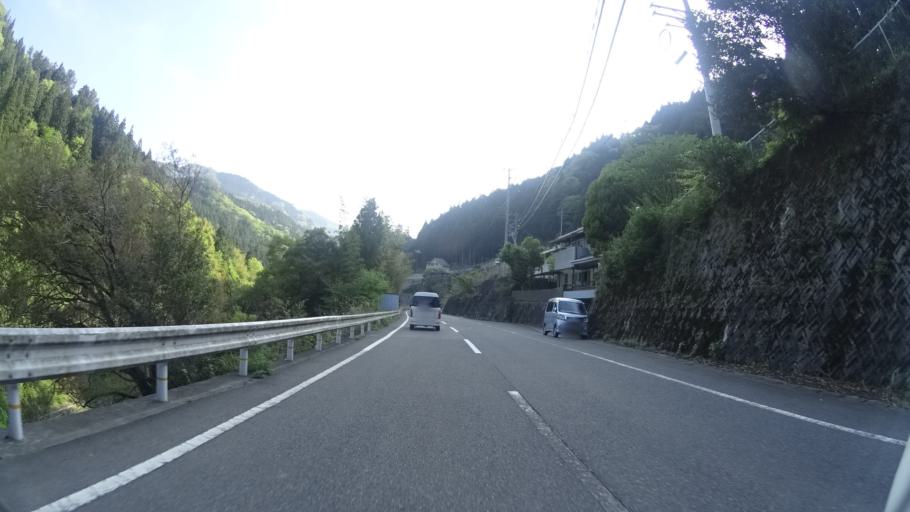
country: JP
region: Tokushima
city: Ikedacho
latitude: 33.8793
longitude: 133.9256
